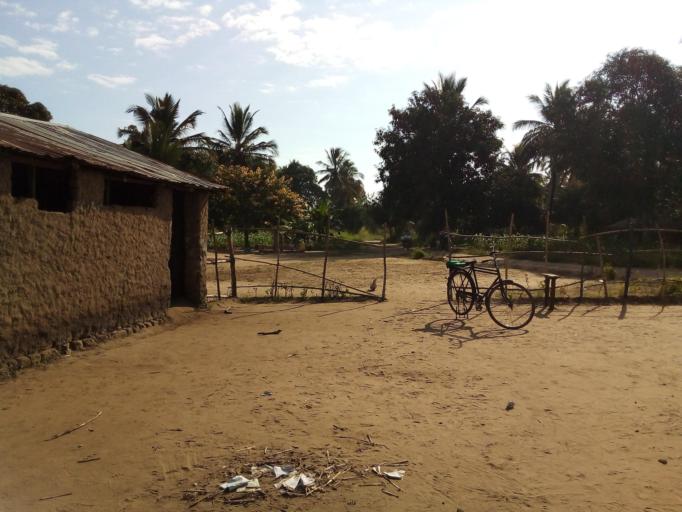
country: MZ
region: Zambezia
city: Quelimane
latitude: -17.6422
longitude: 36.6860
